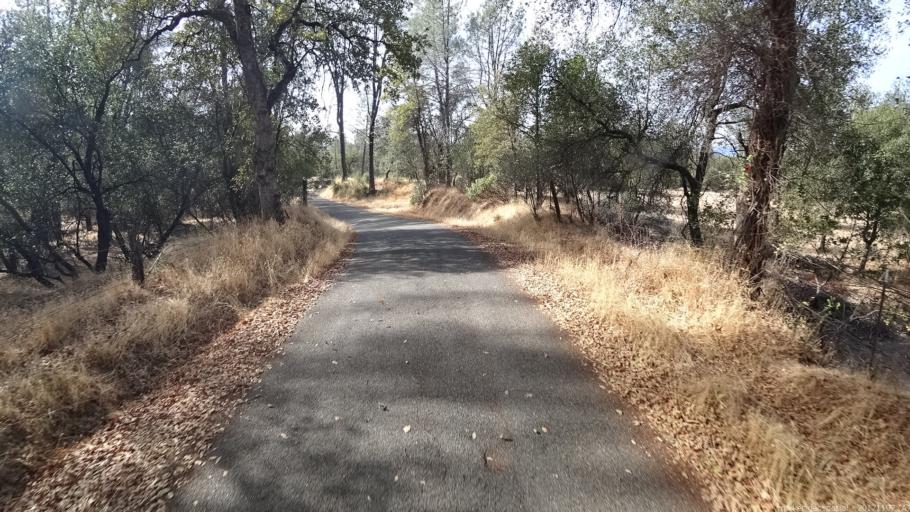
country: US
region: California
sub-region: Shasta County
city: Shasta
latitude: 40.4164
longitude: -122.5291
